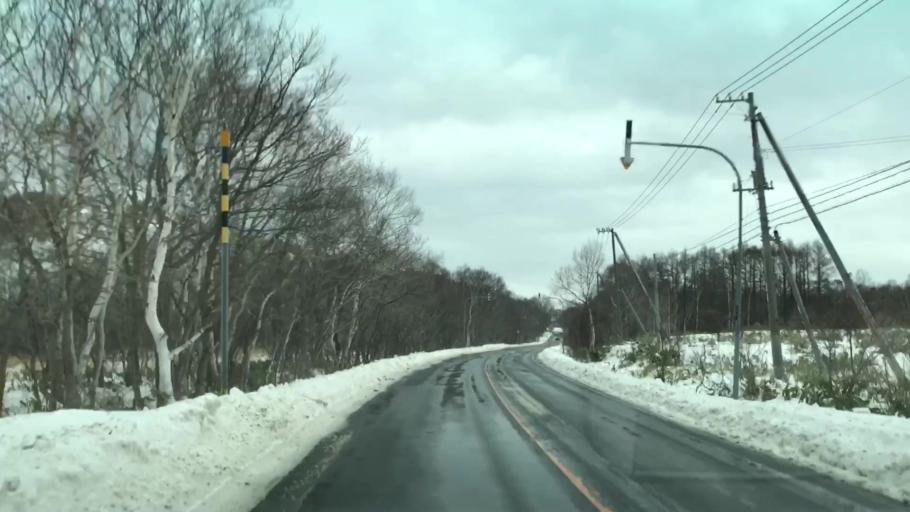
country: JP
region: Hokkaido
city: Yoichi
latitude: 43.3273
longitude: 140.4979
